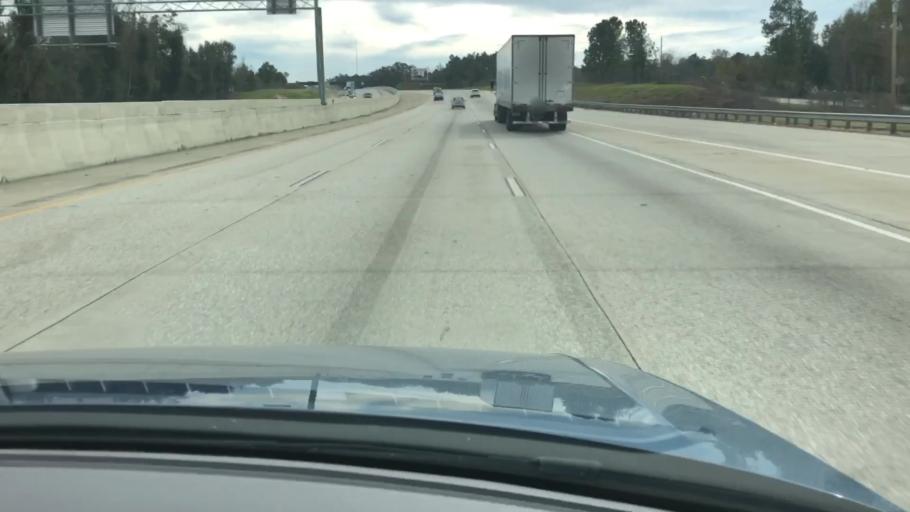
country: US
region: Georgia
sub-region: Crisp County
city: Cordele
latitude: 31.9313
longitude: -83.7468
